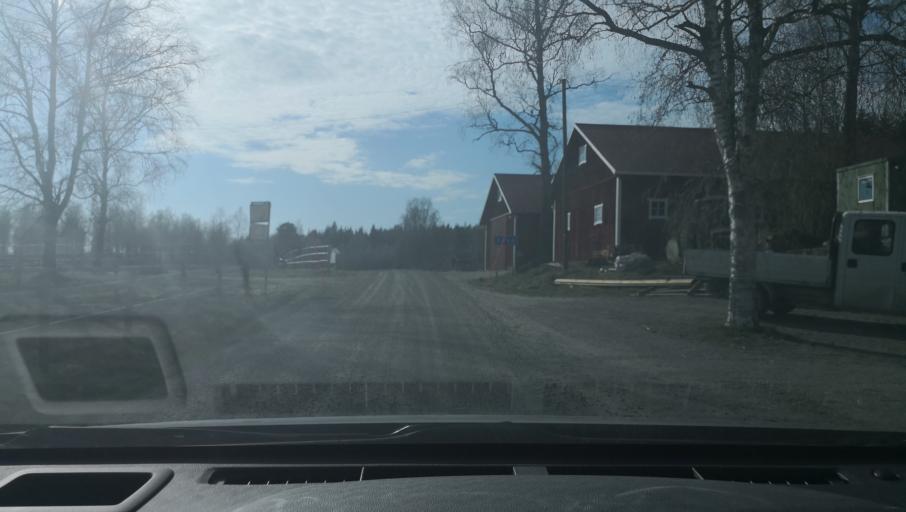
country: SE
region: Uppsala
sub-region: Heby Kommun
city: Morgongava
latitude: 59.8455
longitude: 16.9105
